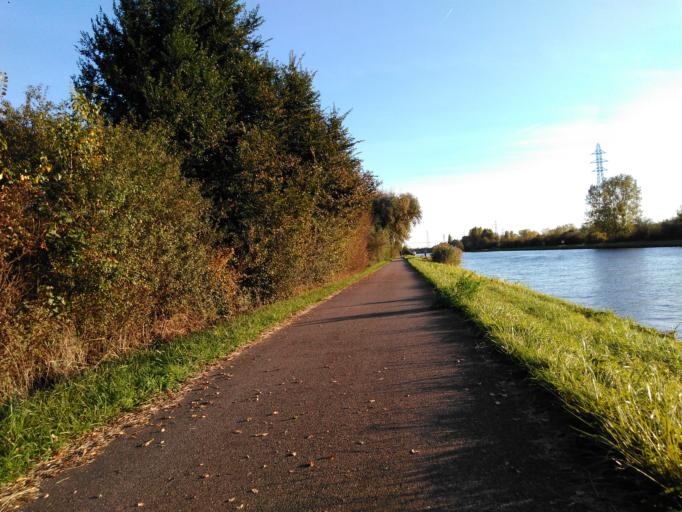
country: FR
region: Lorraine
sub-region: Departement de la Moselle
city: Maizieres-les-Metz
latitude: 49.2124
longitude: 6.1819
